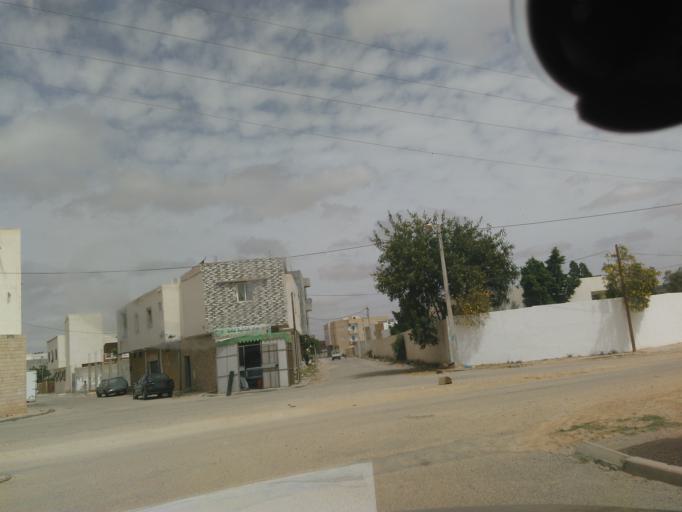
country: TN
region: Tataouine
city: Tataouine
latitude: 32.9499
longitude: 10.4707
